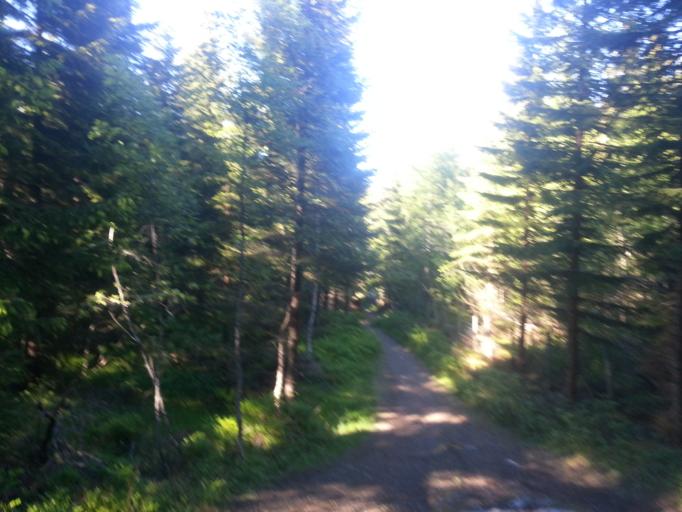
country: NO
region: Sor-Trondelag
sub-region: Trondheim
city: Trondheim
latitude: 63.4230
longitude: 10.3361
